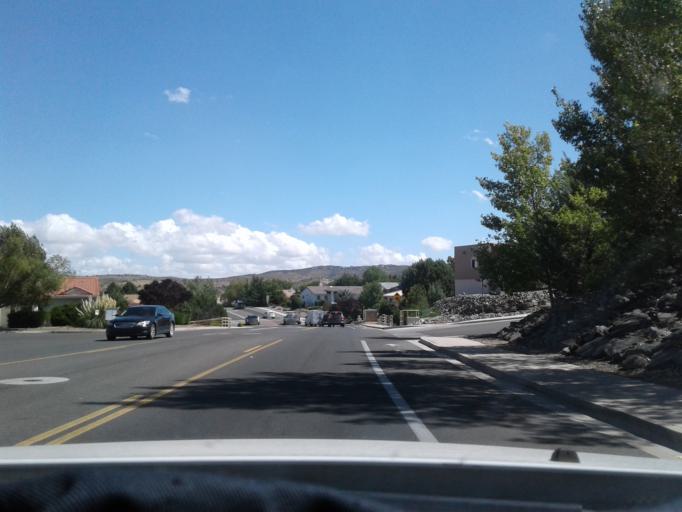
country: US
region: Arizona
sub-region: Yavapai County
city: Prescott
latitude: 34.5736
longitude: -112.4433
